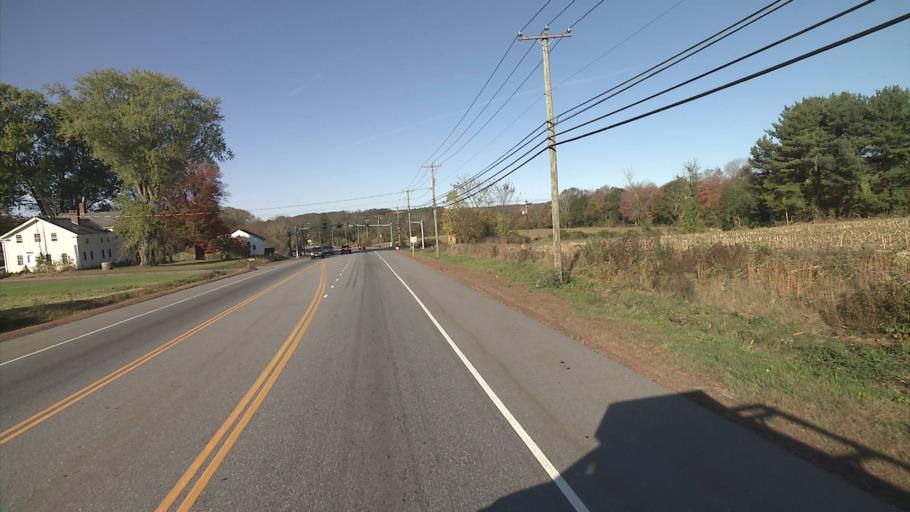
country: US
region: Connecticut
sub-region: Windham County
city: East Brooklyn
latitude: 41.7966
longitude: -71.9261
